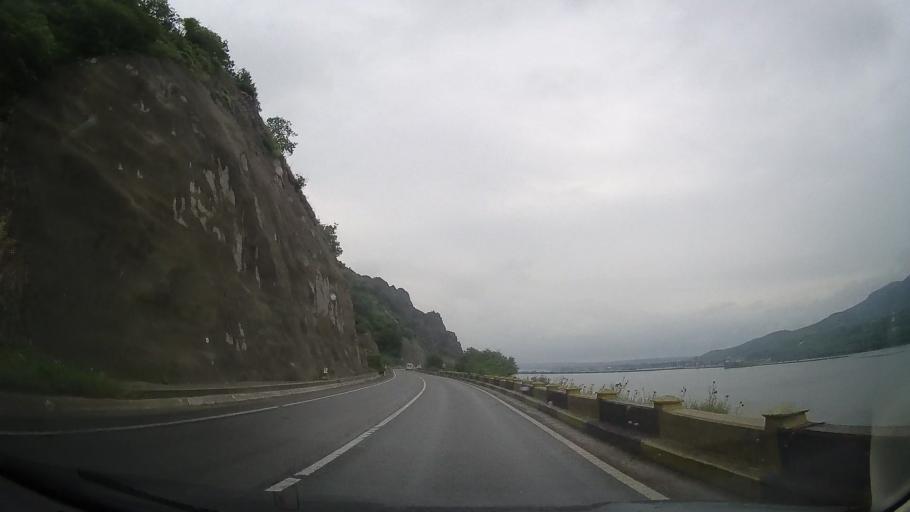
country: RO
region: Mehedinti
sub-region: Municipiul Drobeta-Turnu Severin
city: Gura Vaii
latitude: 44.6842
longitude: 22.5177
